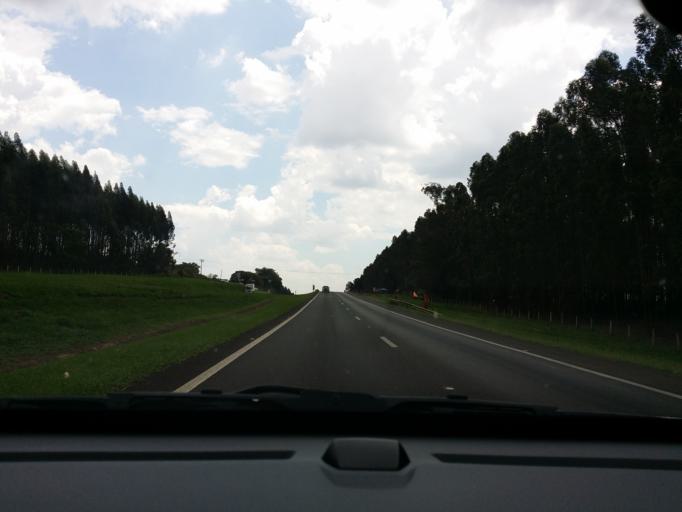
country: BR
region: Sao Paulo
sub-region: Itirapina
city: Itirapina
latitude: -22.2334
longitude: -47.7345
